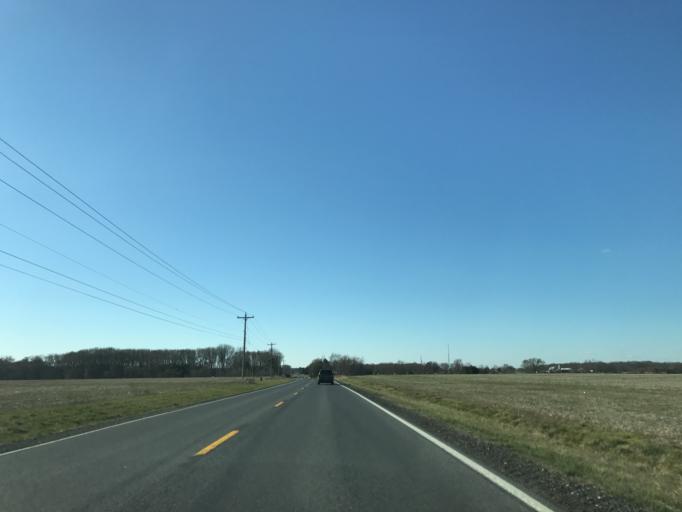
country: US
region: Maryland
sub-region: Queen Anne's County
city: Centreville
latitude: 39.0171
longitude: -76.0038
